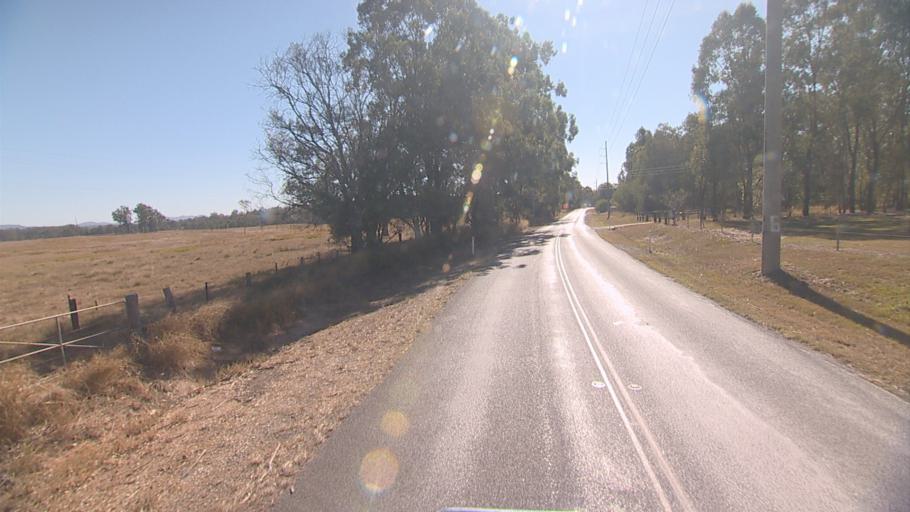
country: AU
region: Queensland
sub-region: Logan
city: Cedar Vale
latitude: -27.8647
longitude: 153.0177
